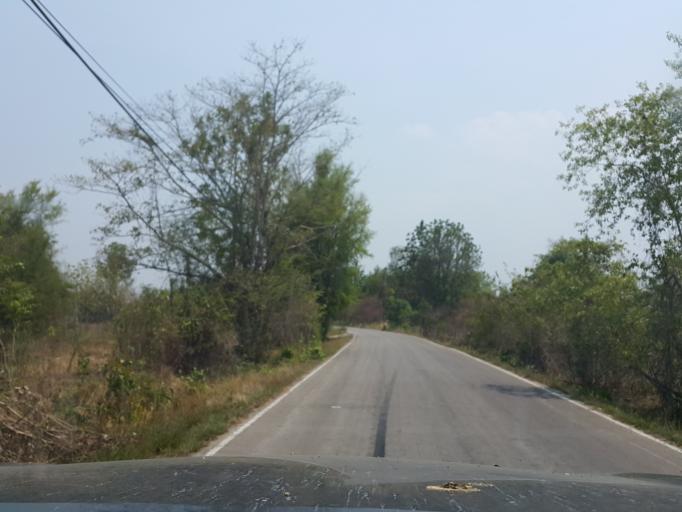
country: TH
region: Lampang
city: Mae Phrik
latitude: 17.5207
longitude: 99.1476
